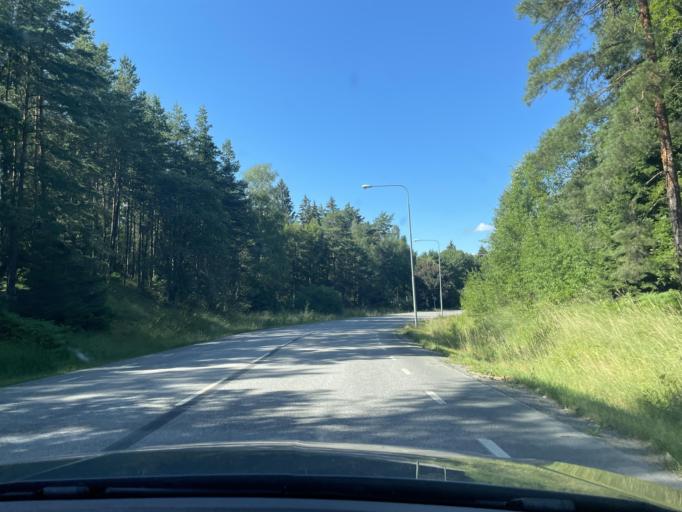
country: SE
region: Stockholm
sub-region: Sigtuna Kommun
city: Marsta
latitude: 59.6202
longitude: 17.8182
